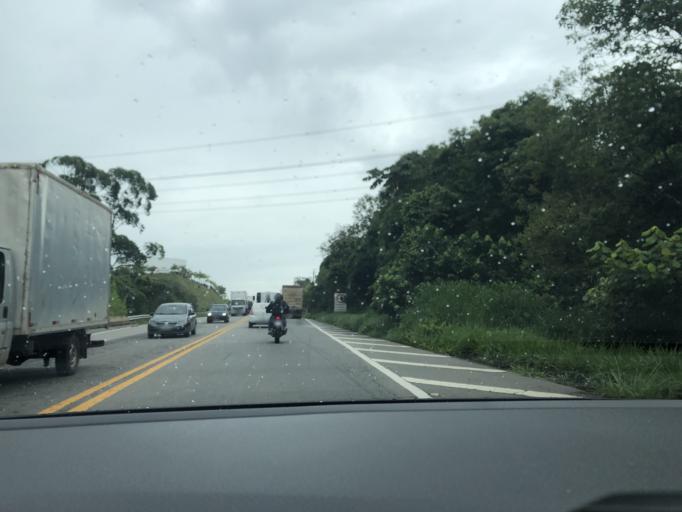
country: BR
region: Sao Paulo
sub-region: Jarinu
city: Jarinu
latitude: -23.1353
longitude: -46.7396
